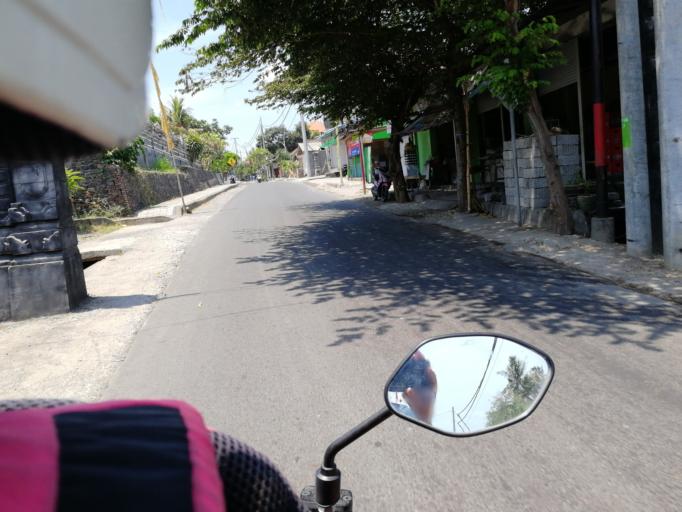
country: ID
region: Bali
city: Banjar Timbrah
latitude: -8.4800
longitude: 115.5975
